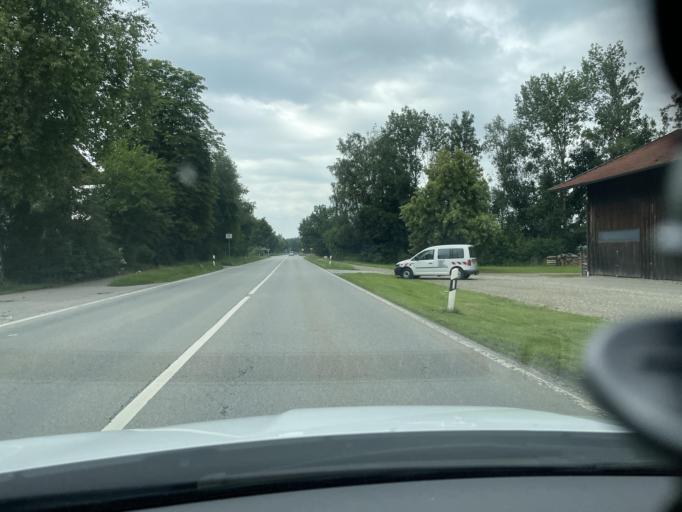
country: DE
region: Bavaria
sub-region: Upper Bavaria
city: Soyen
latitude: 48.0948
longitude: 12.1946
